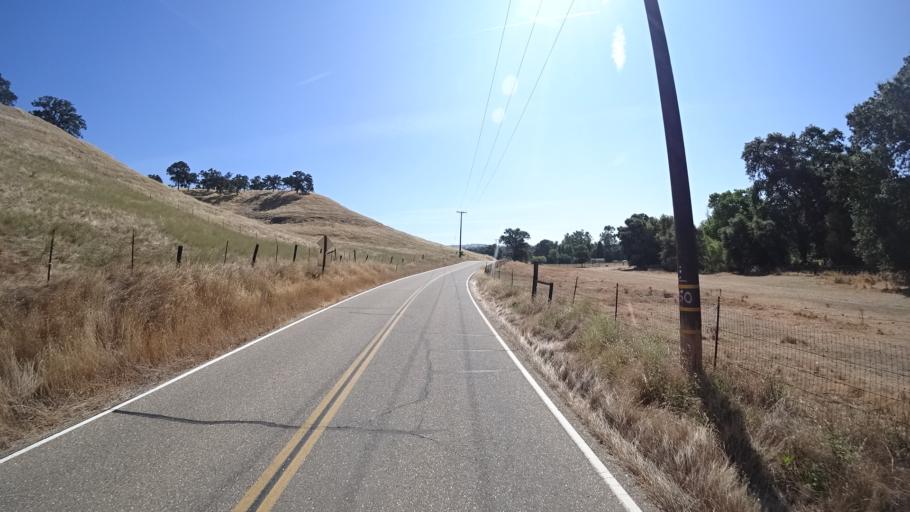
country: US
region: California
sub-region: Calaveras County
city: Rancho Calaveras
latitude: 38.0989
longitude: -120.8831
